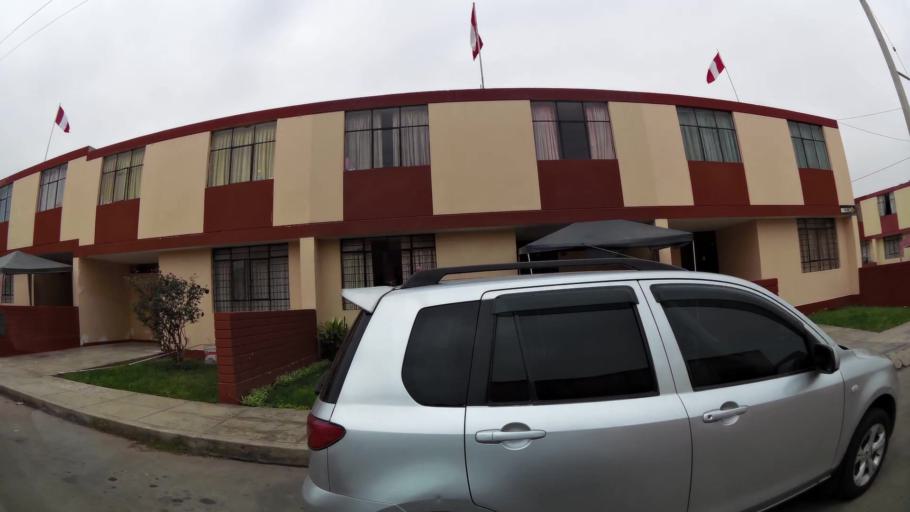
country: PE
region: Lima
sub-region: Lima
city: Surco
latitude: -12.1586
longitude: -77.0195
